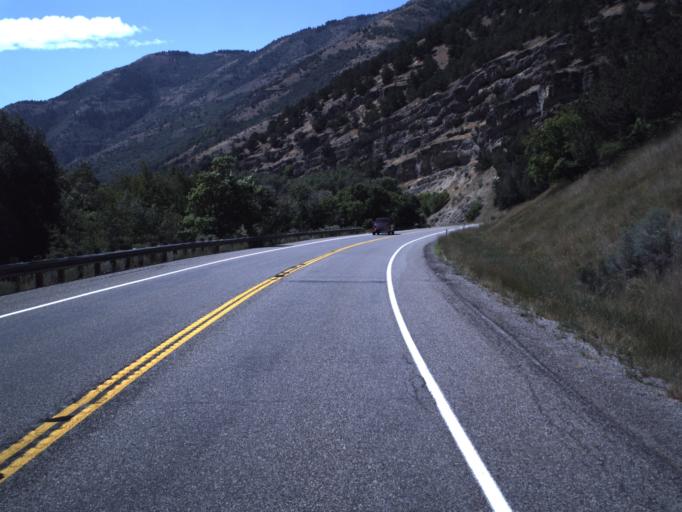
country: US
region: Utah
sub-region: Cache County
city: North Logan
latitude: 41.7653
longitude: -111.6811
